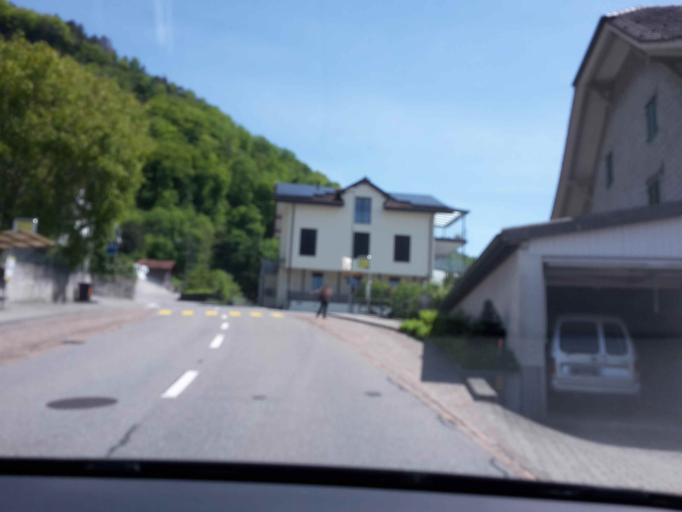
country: CH
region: Bern
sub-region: Thun District
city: Steffisburg
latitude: 46.7621
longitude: 7.6362
